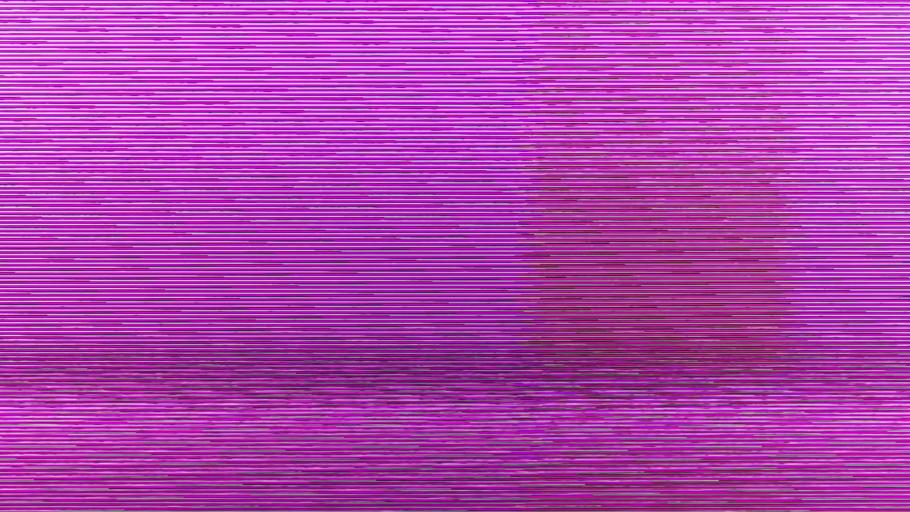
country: US
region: Michigan
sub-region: Oakland County
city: Lake Orion
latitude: 42.7467
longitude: -83.2463
